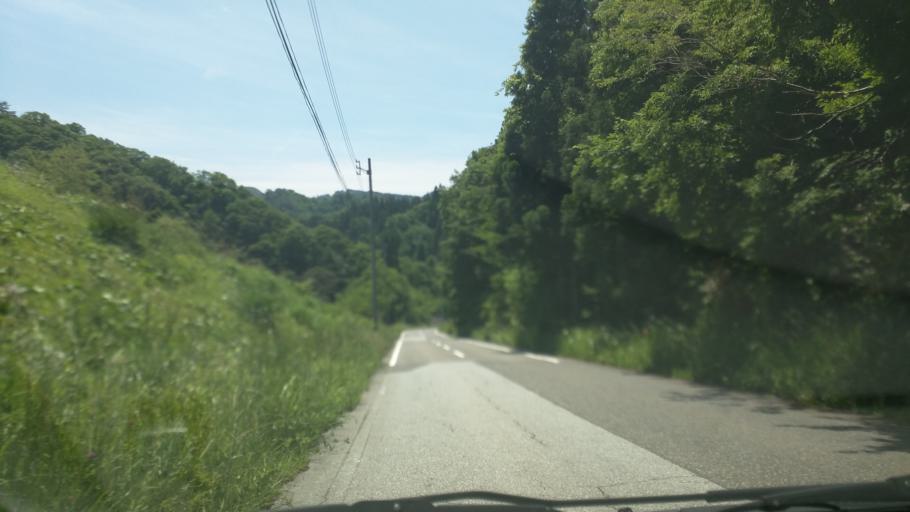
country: JP
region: Fukushima
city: Kitakata
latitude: 37.5059
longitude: 139.7419
